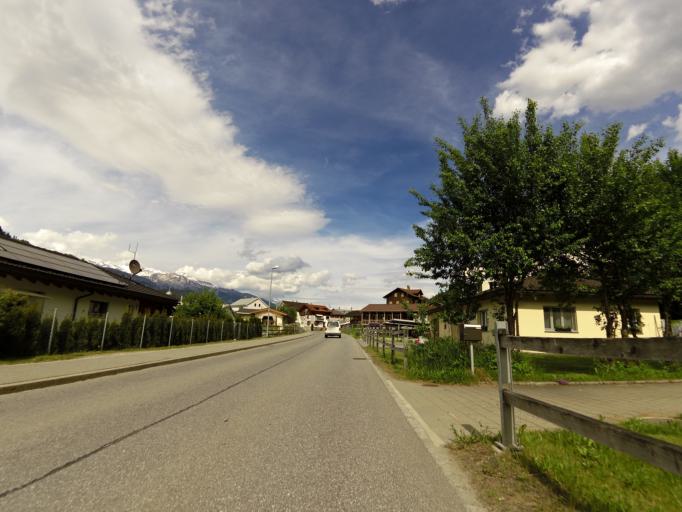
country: CH
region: Grisons
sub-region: Surselva District
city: Ilanz
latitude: 46.7754
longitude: 9.2295
